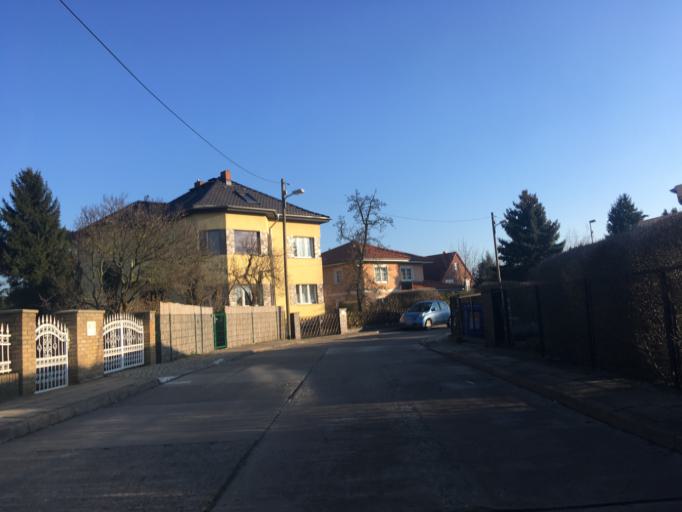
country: DE
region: Berlin
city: Heinersdorf
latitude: 52.5692
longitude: 13.4304
